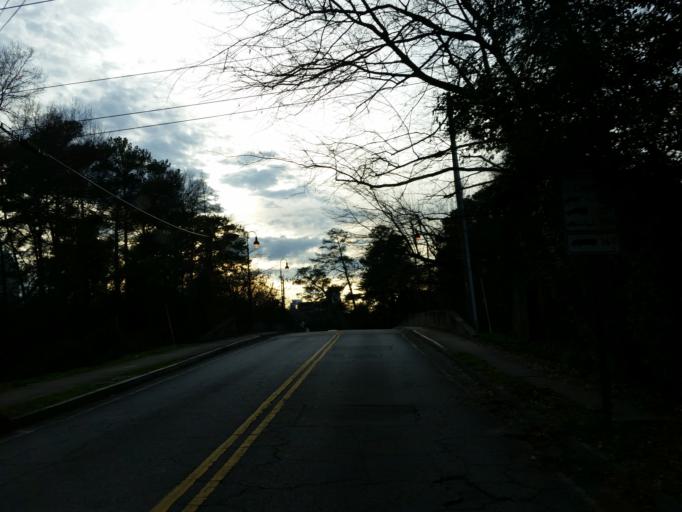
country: US
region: Georgia
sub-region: DeKalb County
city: Druid Hills
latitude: 33.8014
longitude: -84.3736
